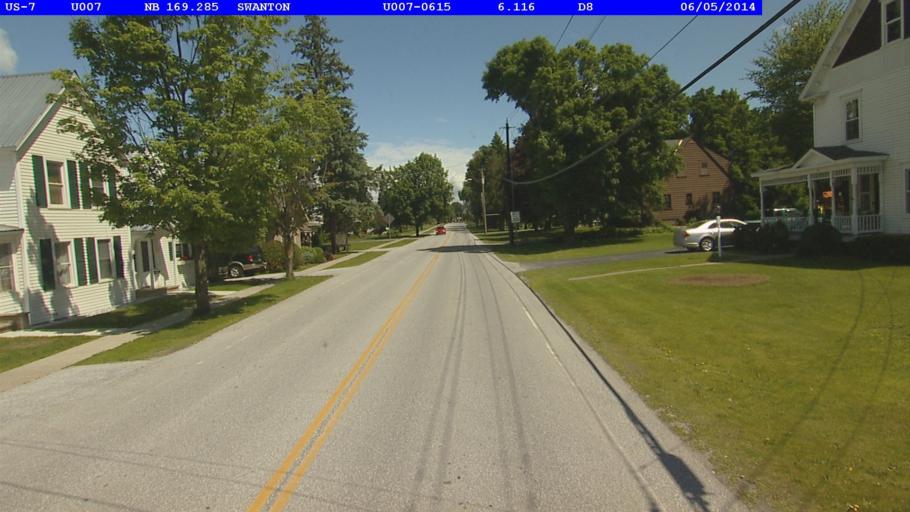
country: US
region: Vermont
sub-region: Franklin County
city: Swanton
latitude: 44.9212
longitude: -73.1215
